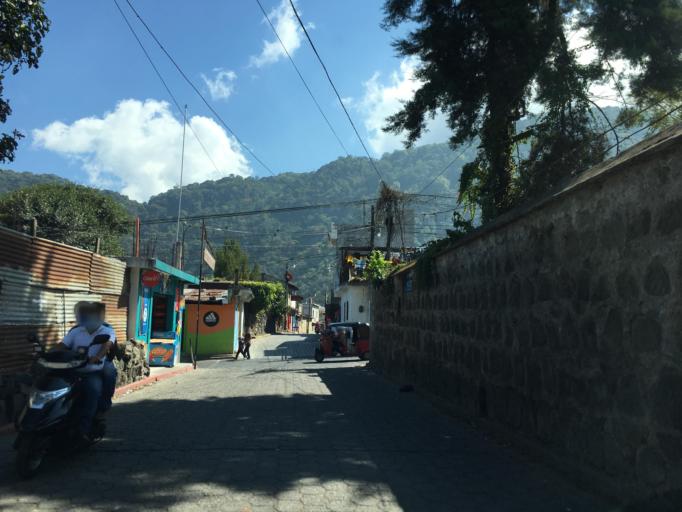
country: GT
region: Solola
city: San Lucas Toliman
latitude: 14.6354
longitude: -91.1427
